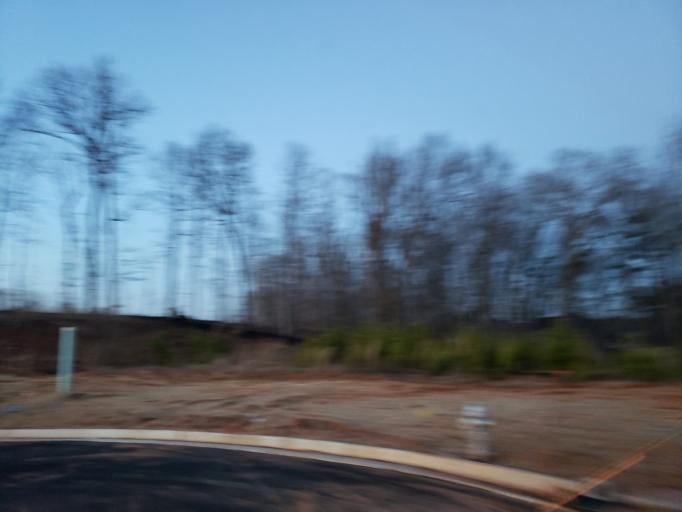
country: US
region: Georgia
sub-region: Cobb County
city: Powder Springs
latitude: 33.9337
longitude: -84.6915
